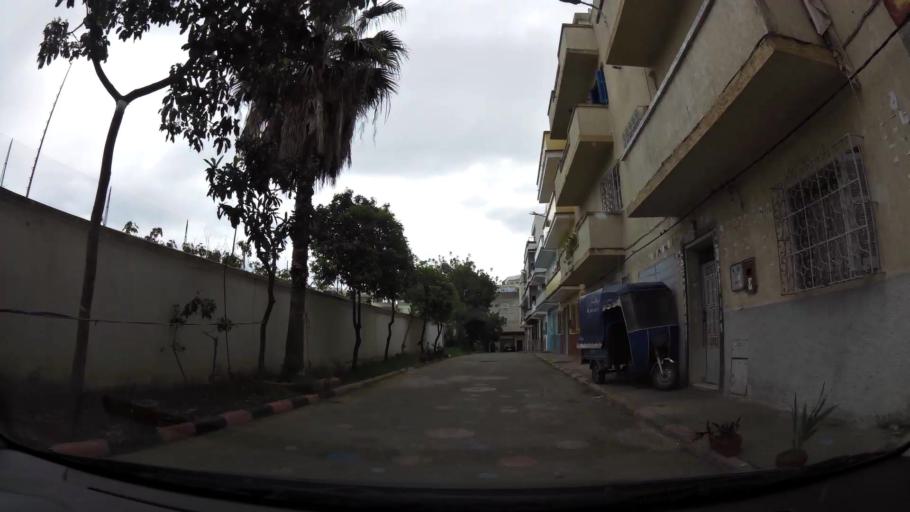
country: MA
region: Tanger-Tetouan
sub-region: Tanger-Assilah
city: Tangier
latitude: 35.7725
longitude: -5.8183
